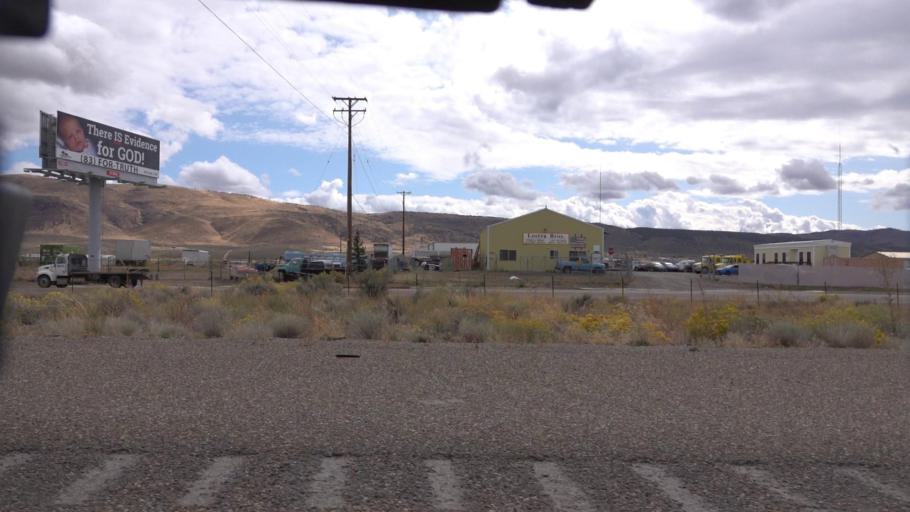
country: US
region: Nevada
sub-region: Elko County
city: Elko
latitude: 40.8766
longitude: -115.7211
